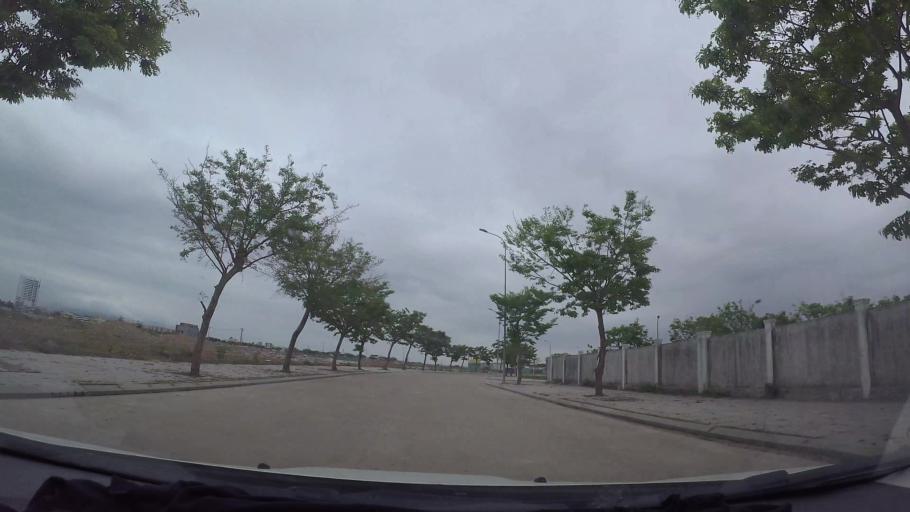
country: VN
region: Da Nang
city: Lien Chieu
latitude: 16.1058
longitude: 108.1205
